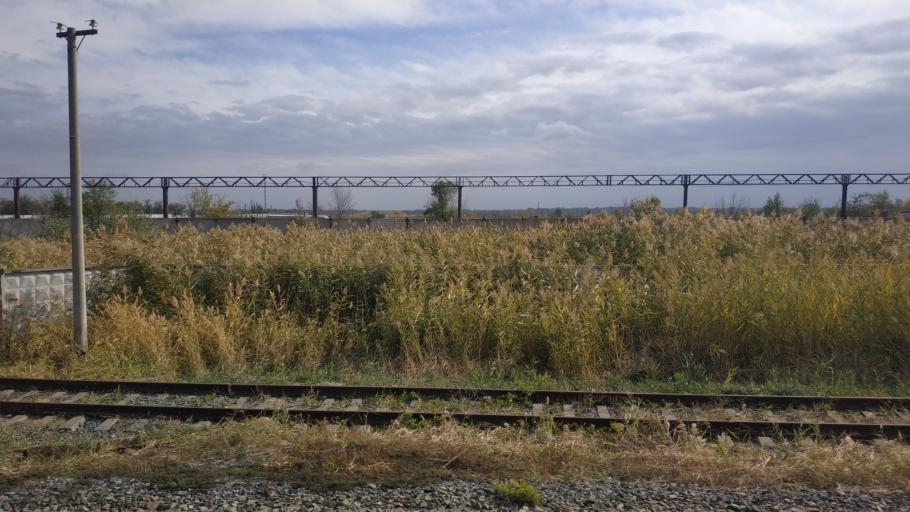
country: RU
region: Volgograd
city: Volgograd
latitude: 48.5930
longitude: 44.4334
